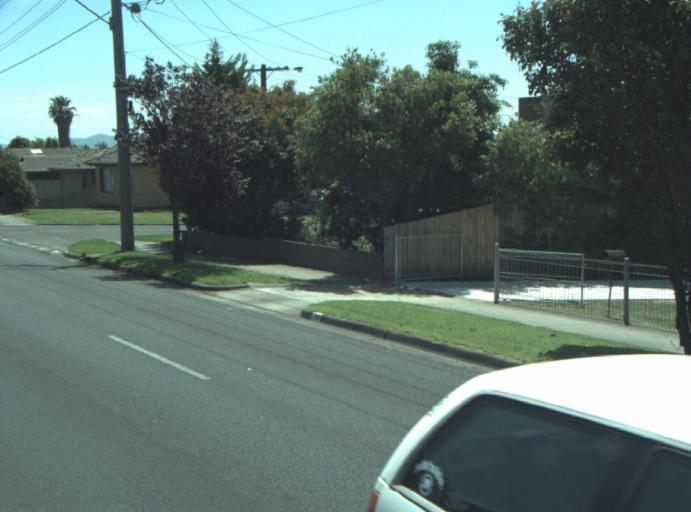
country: AU
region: Victoria
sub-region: Greater Geelong
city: Bell Park
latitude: -38.1044
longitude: 144.3328
